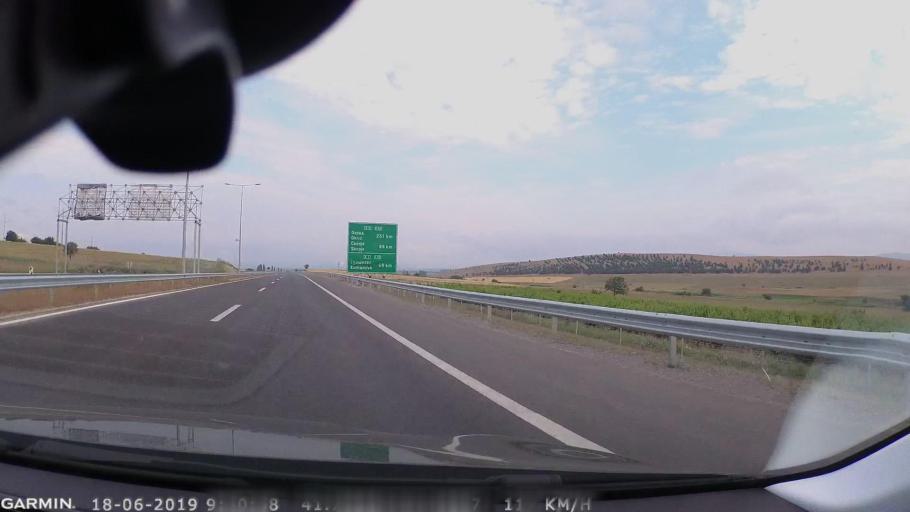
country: MK
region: Stip
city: Shtip
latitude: 41.7844
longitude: 22.1207
